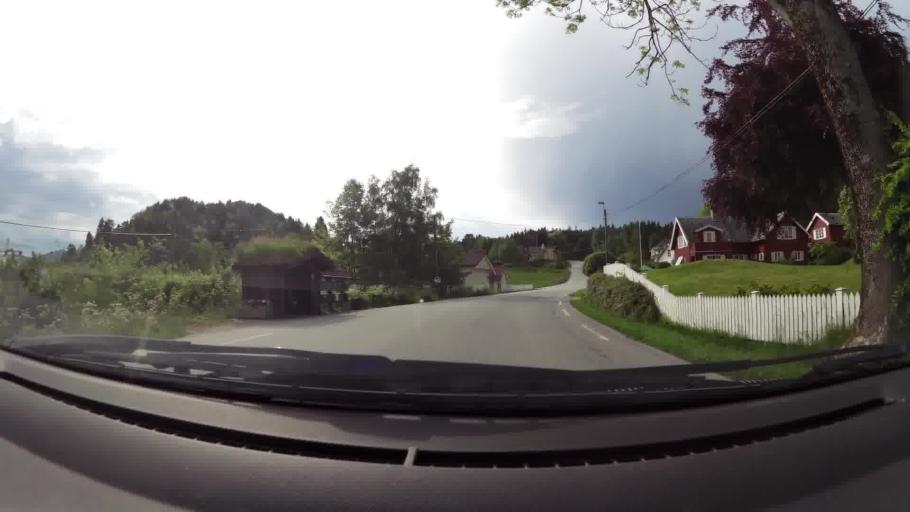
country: NO
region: More og Romsdal
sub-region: Kristiansund
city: Kristiansund
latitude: 63.0292
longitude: 7.7532
